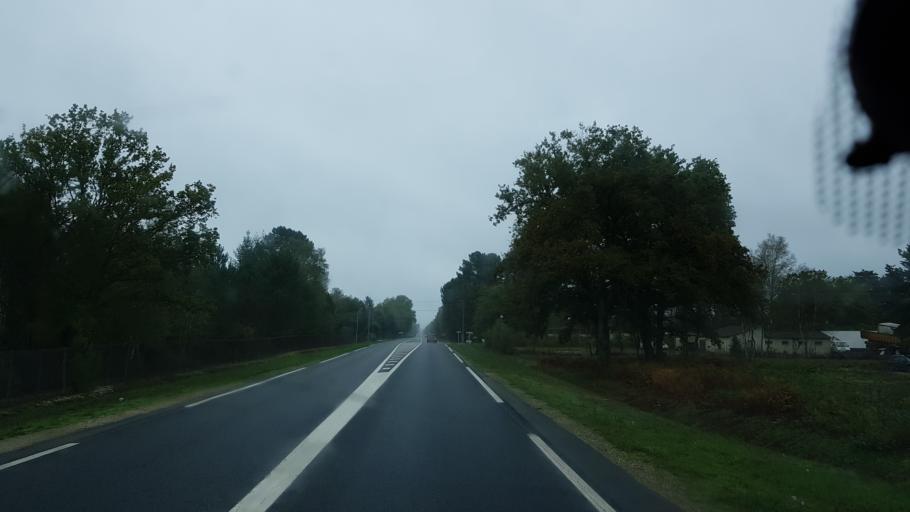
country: FR
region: Centre
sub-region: Departement du Loir-et-Cher
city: Salbris
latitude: 47.4469
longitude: 2.0449
